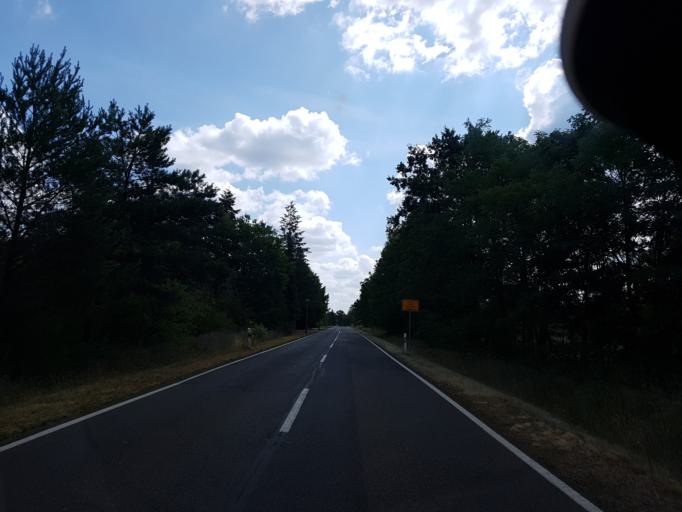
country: DE
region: Brandenburg
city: Altdobern
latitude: 51.6875
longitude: 14.1178
